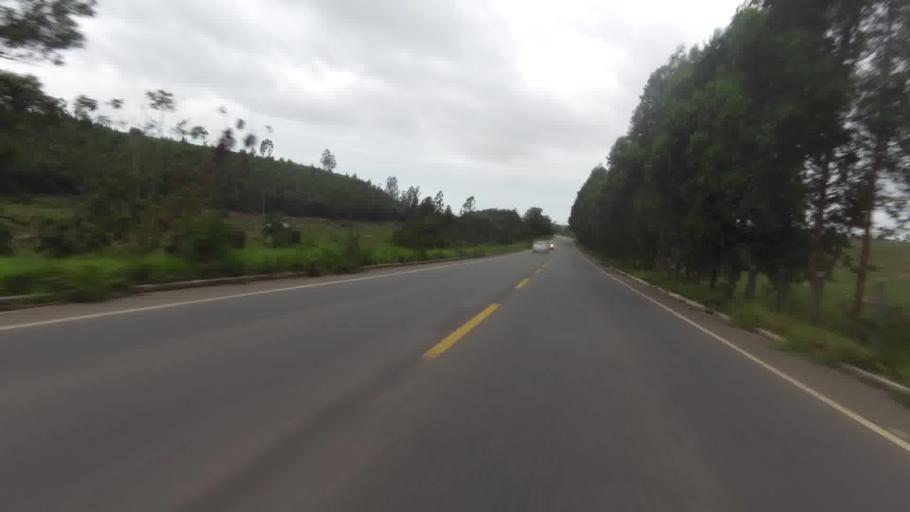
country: BR
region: Espirito Santo
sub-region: Piuma
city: Piuma
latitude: -20.7946
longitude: -40.7502
